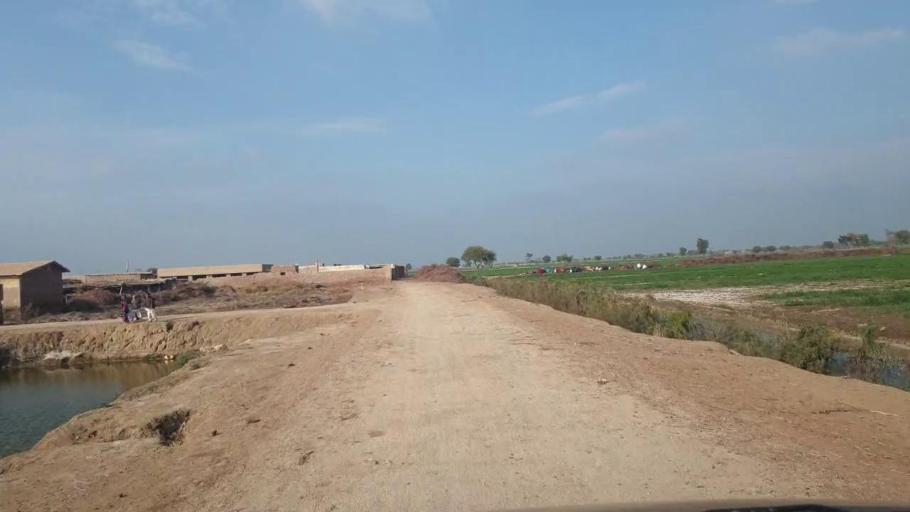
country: PK
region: Sindh
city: Shahdadpur
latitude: 25.8987
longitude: 68.6706
